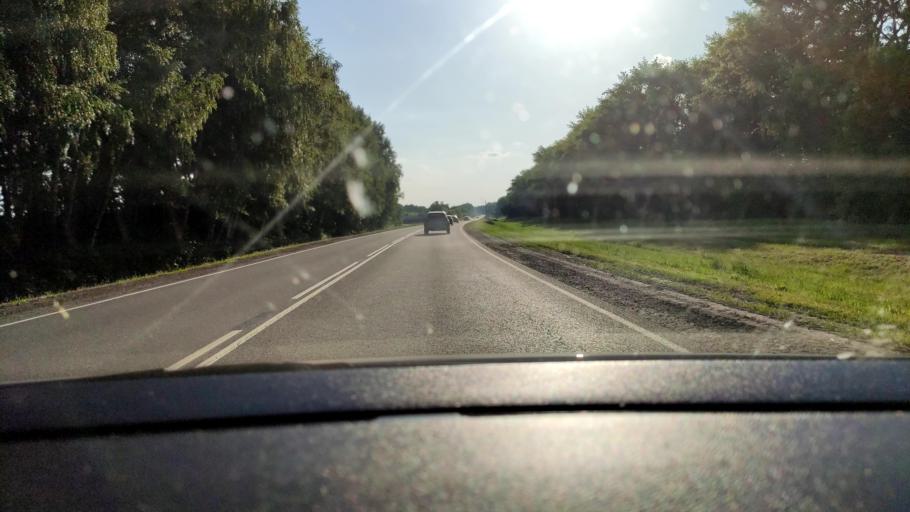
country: RU
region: Voronezj
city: Kashirskoye
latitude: 51.4579
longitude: 39.8159
